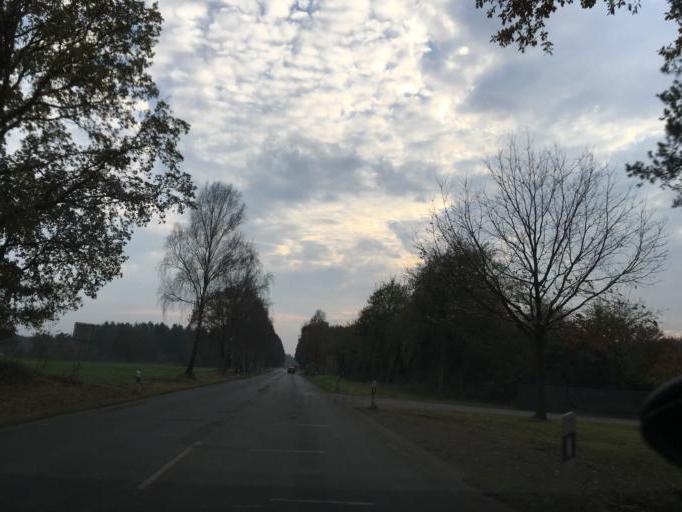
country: DE
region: Lower Saxony
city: Wietzendorf
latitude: 52.9684
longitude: 9.9792
